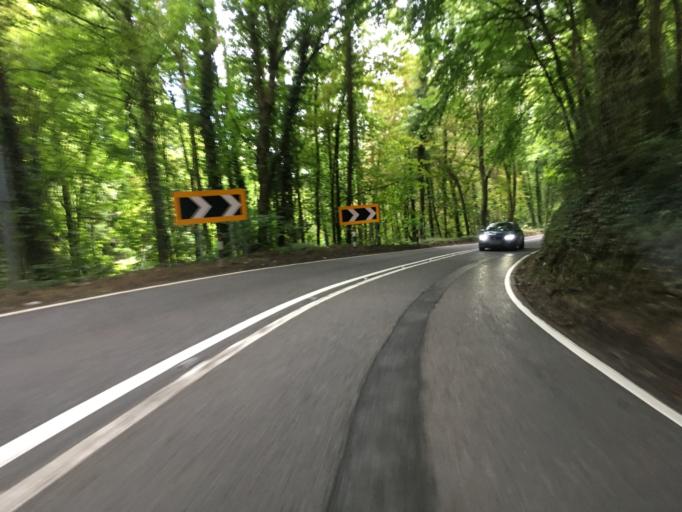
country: GB
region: England
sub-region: Hampshire
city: Petersfield
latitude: 51.0139
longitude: -1.0034
